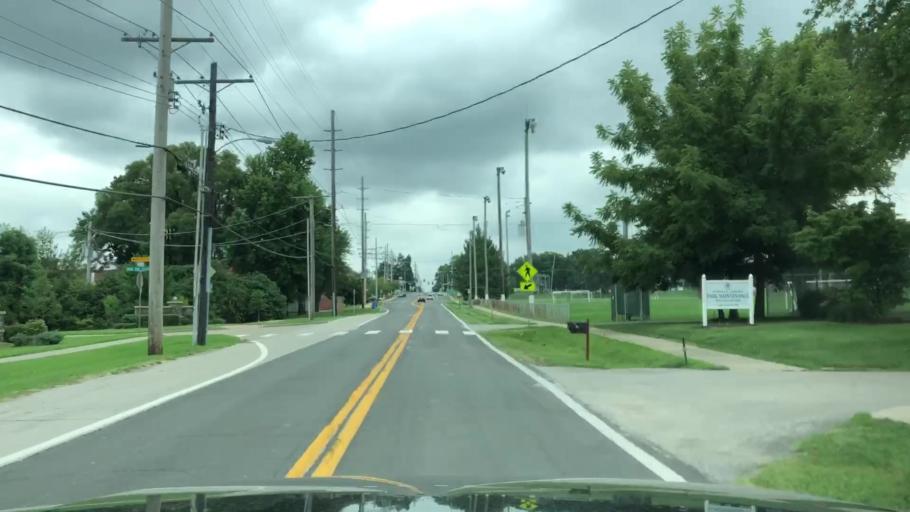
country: US
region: Missouri
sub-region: Saint Louis County
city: Hazelwood
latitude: 38.8108
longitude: -90.3621
